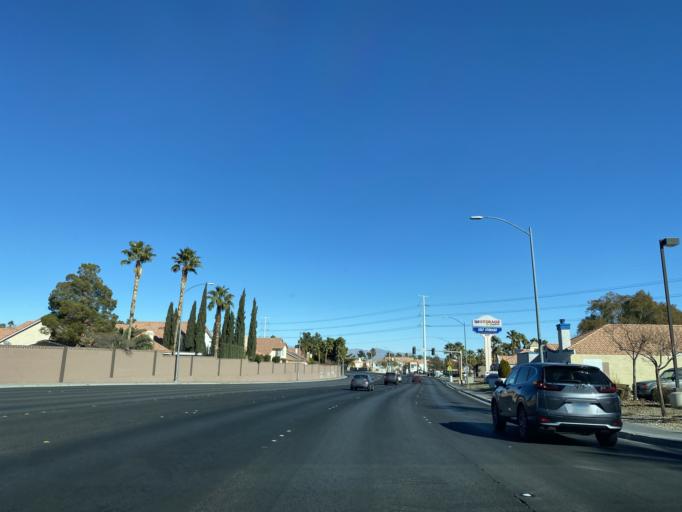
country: US
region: Nevada
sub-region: Clark County
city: Spring Valley
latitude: 36.1609
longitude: -115.2798
